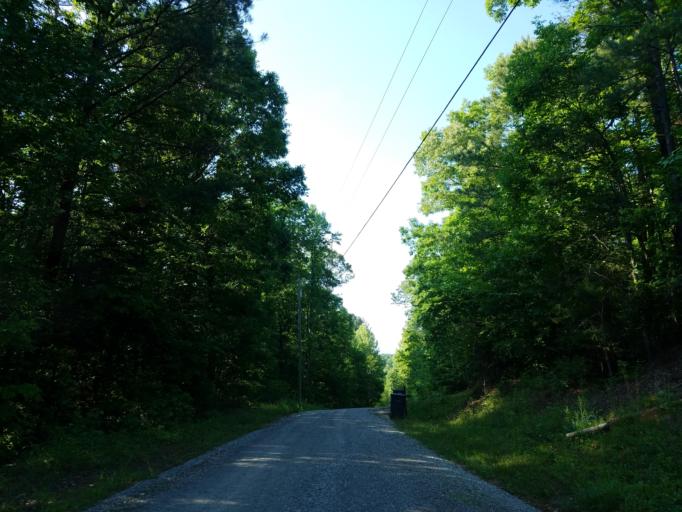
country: US
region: Georgia
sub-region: Pickens County
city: Nelson
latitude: 34.3603
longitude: -84.3484
